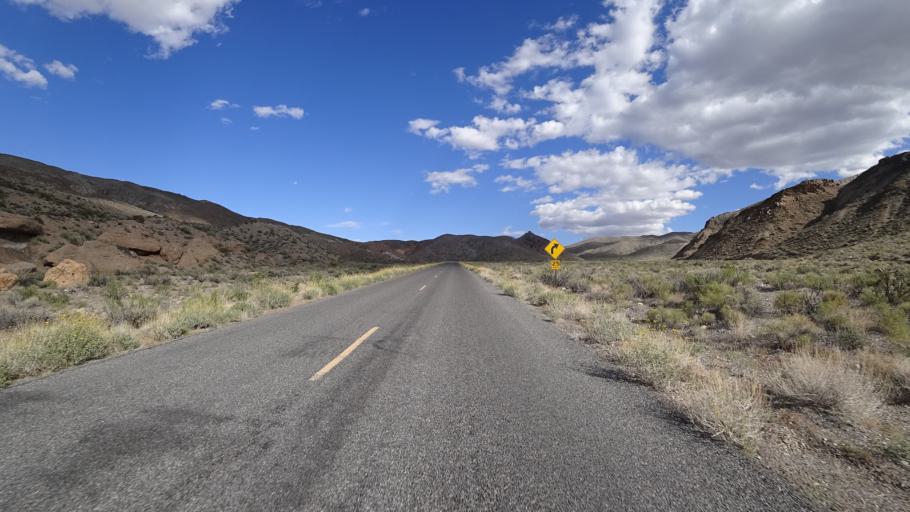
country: US
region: Nevada
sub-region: Nye County
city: Beatty
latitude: 36.4233
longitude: -117.1900
